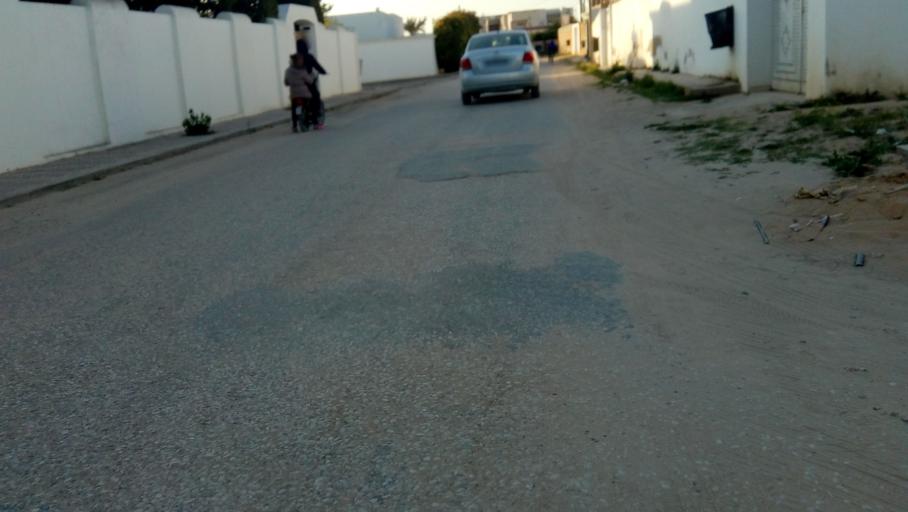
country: TN
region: Safaqis
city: Sfax
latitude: 34.7524
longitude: 10.7344
